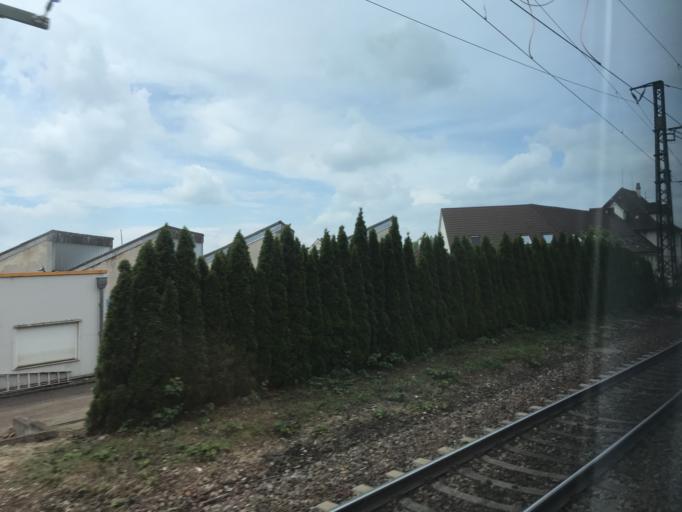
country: DE
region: Baden-Wuerttemberg
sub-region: Regierungsbezirk Stuttgart
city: Sussen
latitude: 48.6799
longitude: 9.7660
